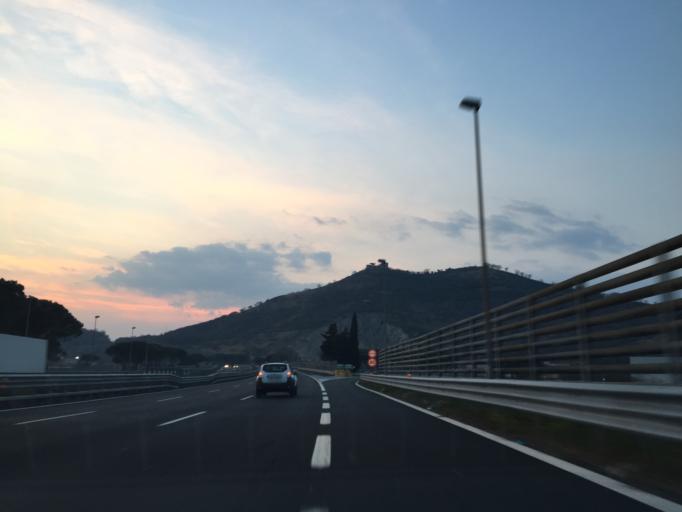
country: IT
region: Campania
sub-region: Provincia di Salerno
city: Lanzara
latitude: 40.7705
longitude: 14.6702
